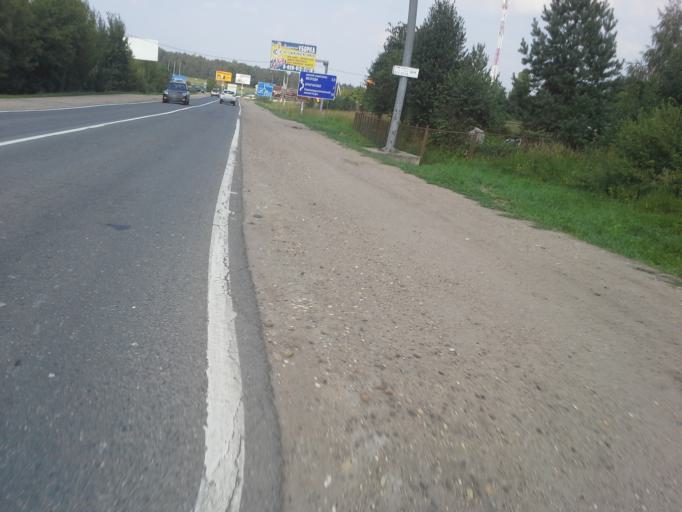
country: RU
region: Moskovskaya
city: Istra
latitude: 55.8593
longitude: 36.7941
